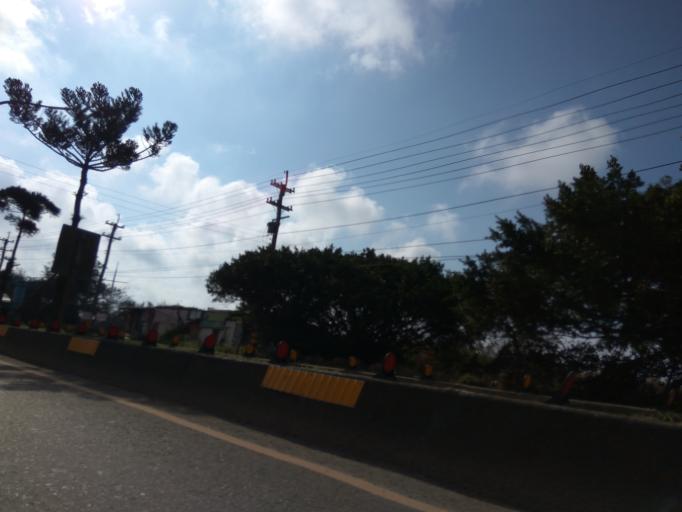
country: TW
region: Taiwan
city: Taoyuan City
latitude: 25.0398
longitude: 121.1034
